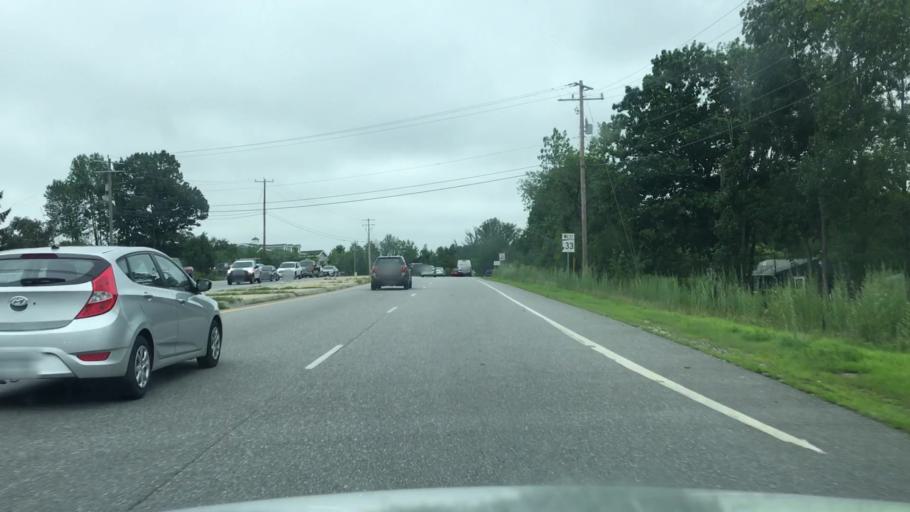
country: US
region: New Hampshire
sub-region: Rockingham County
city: Greenland
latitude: 43.0442
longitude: -70.8194
